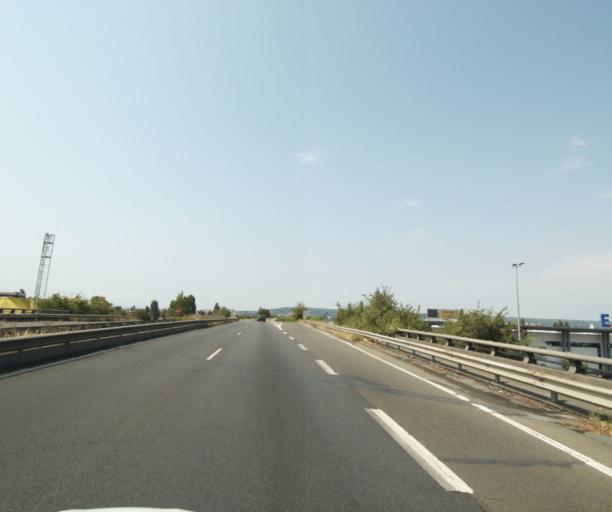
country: FR
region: Ile-de-France
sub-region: Departement des Yvelines
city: Conflans-Sainte-Honorine
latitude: 49.0083
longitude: 2.0867
